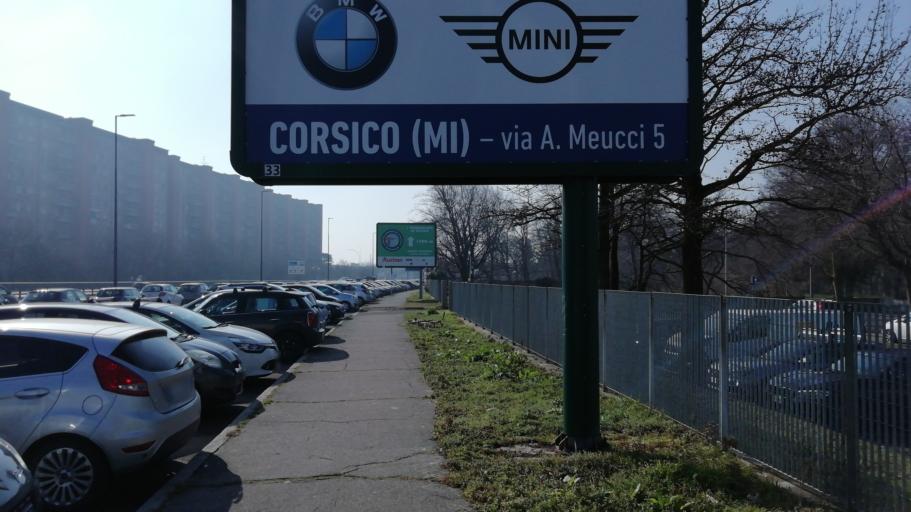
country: IT
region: Lombardy
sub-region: Citta metropolitana di Milano
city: Corsico
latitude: 45.4398
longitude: 9.1088
